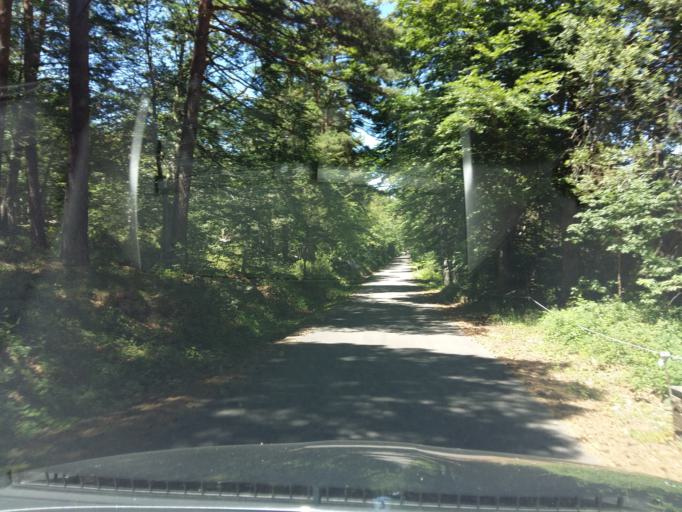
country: ES
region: Castille and Leon
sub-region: Provincia de Soria
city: Vozmediano
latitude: 41.8032
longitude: -1.8119
